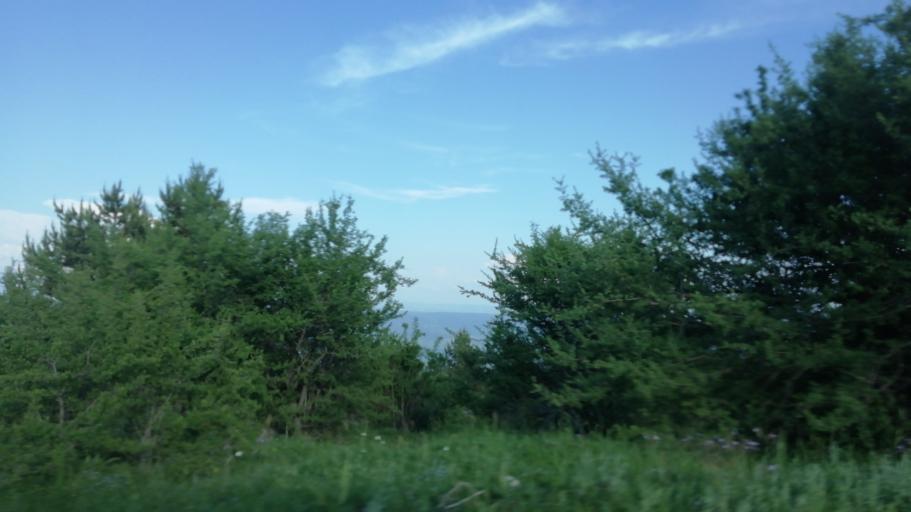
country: TR
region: Karabuk
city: Eskipazar
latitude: 41.0472
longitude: 32.5594
